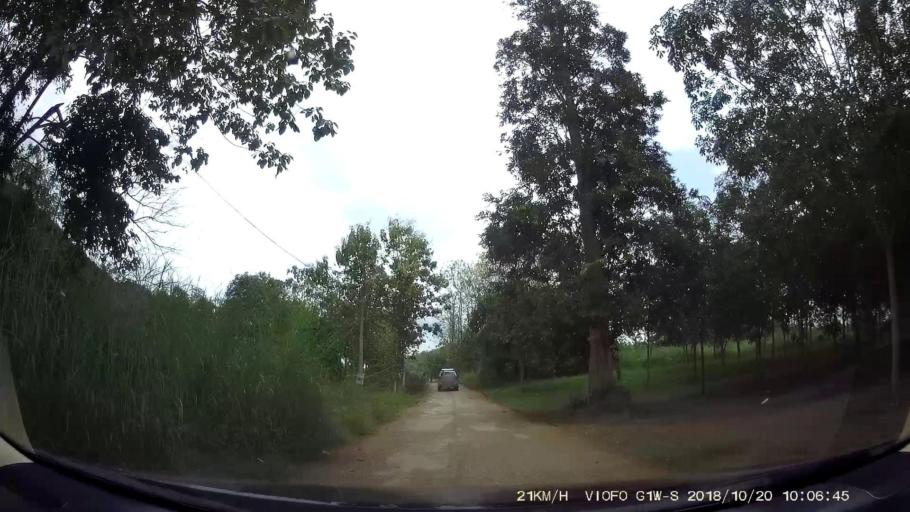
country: TH
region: Chaiyaphum
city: Khon San
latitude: 16.5456
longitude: 101.8521
